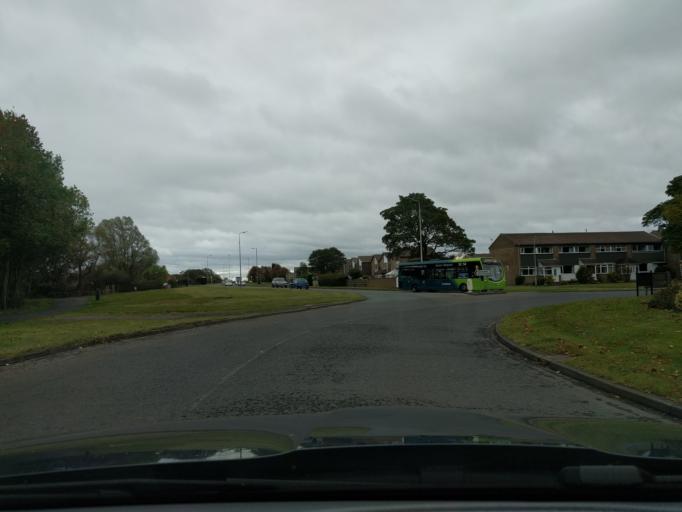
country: GB
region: England
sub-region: Northumberland
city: Cramlington
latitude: 55.0825
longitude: -1.5873
